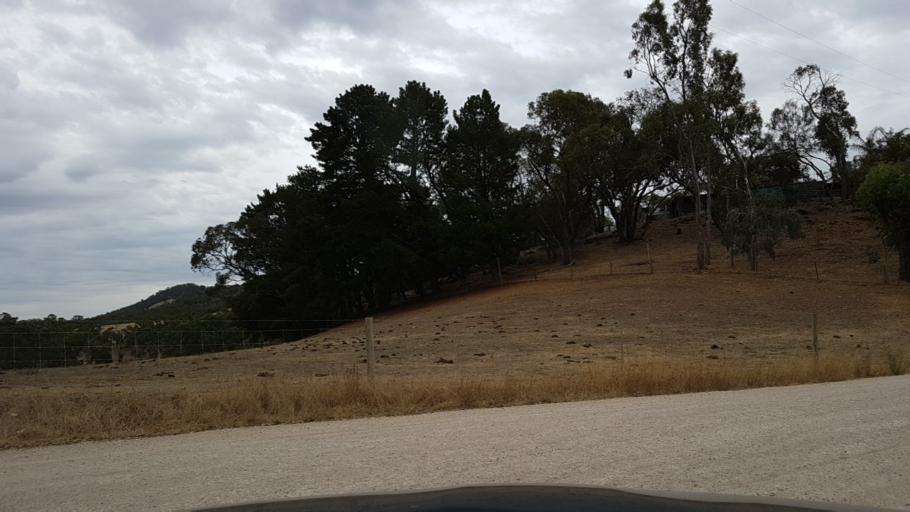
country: AU
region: South Australia
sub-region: Tea Tree Gully
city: Golden Grove
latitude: -34.8024
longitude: 138.8063
